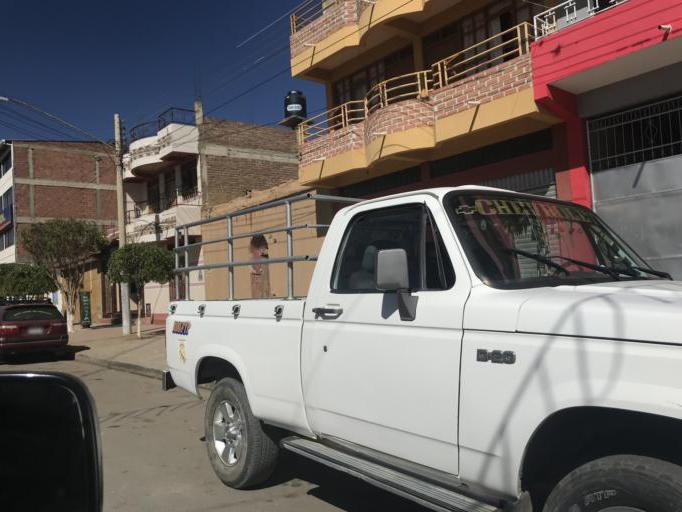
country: BO
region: Cochabamba
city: Cliza
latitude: -17.5909
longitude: -65.9331
